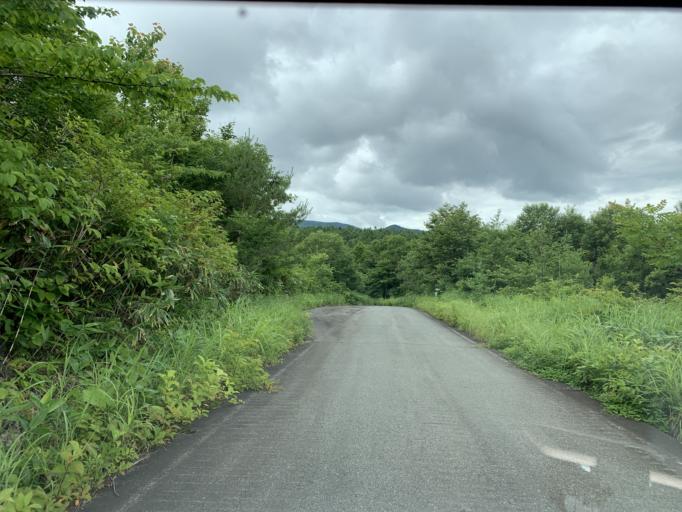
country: JP
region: Iwate
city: Ichinoseki
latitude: 38.9348
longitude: 140.8798
